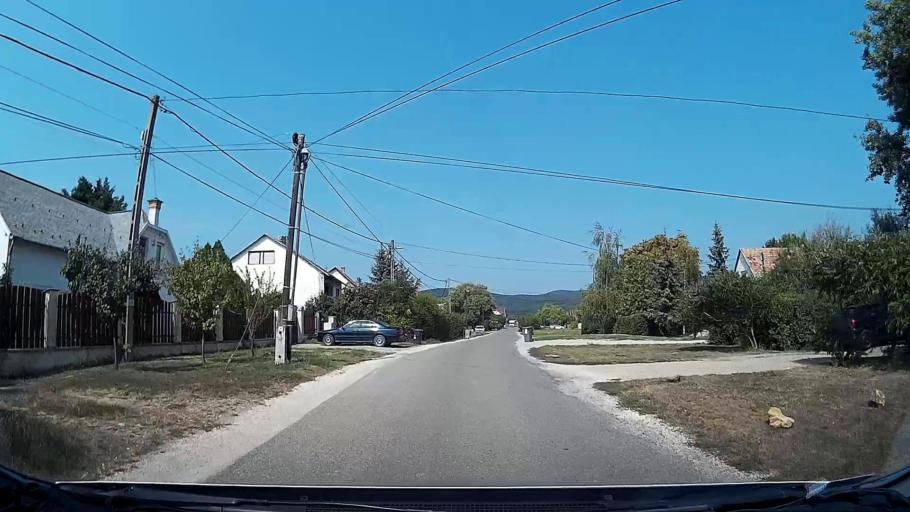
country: HU
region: Pest
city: Szentendre
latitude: 47.6870
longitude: 19.0453
